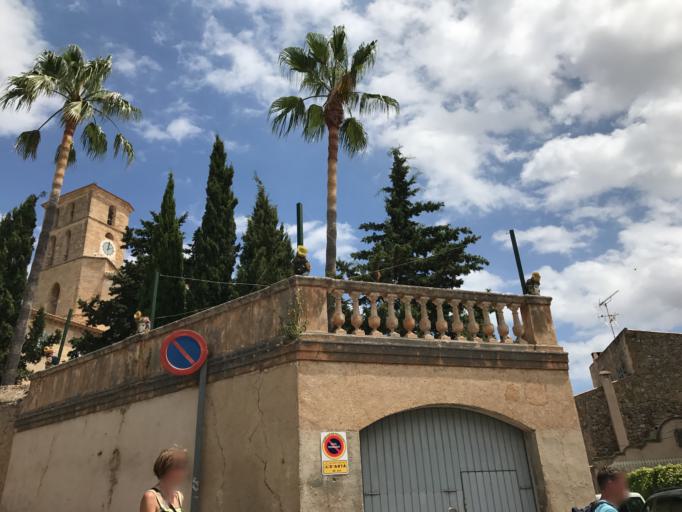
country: ES
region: Balearic Islands
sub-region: Illes Balears
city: Arta
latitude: 39.6954
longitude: 3.3517
